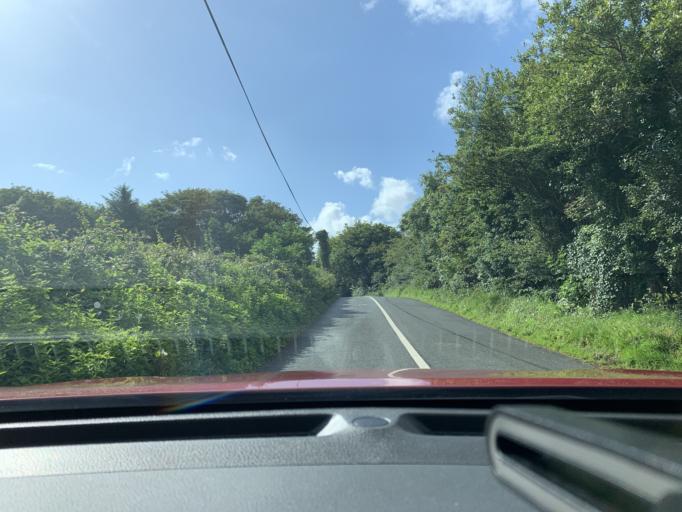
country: IE
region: Connaught
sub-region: Sligo
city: Strandhill
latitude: 54.3577
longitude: -8.6105
